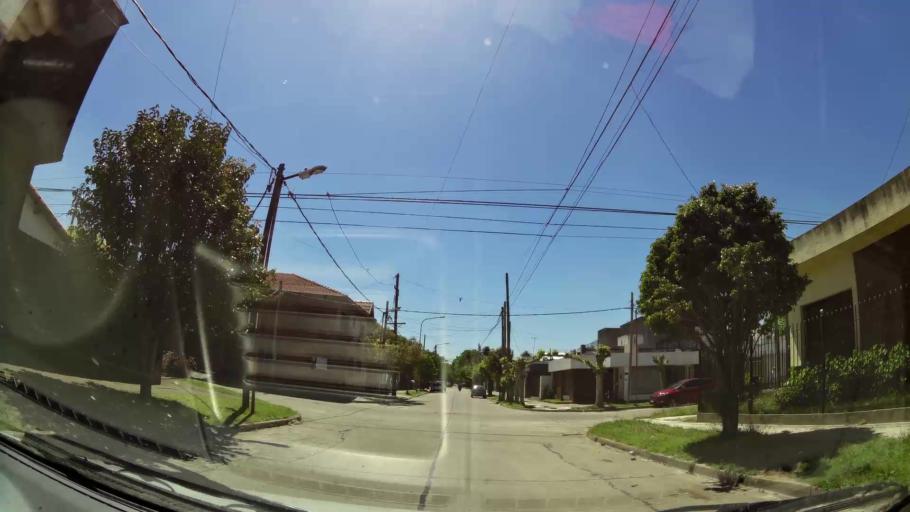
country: AR
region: Buenos Aires
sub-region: Partido de Quilmes
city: Quilmes
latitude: -34.7268
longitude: -58.2723
